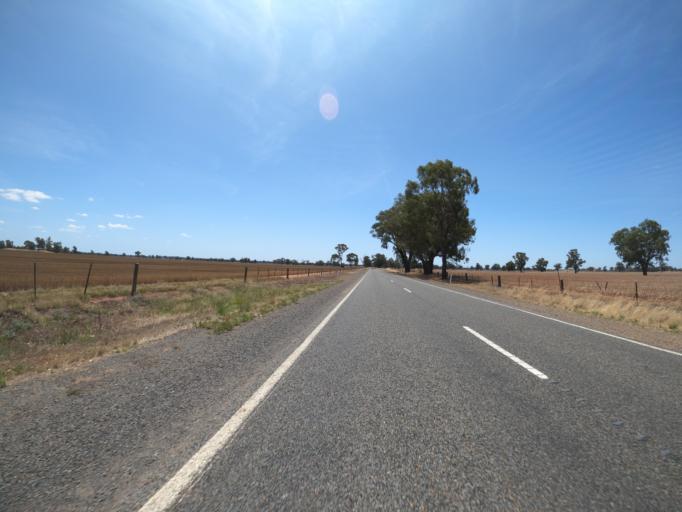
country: AU
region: Victoria
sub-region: Moira
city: Yarrawonga
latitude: -36.2148
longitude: 145.9672
